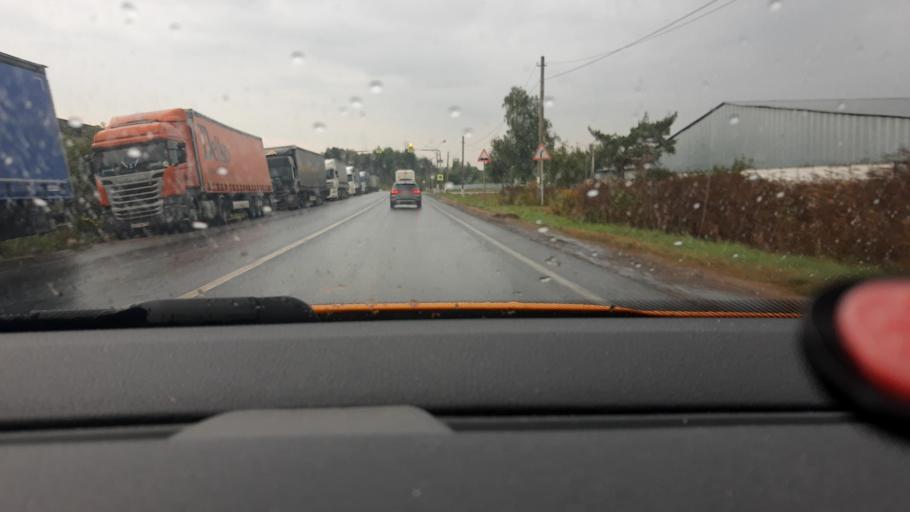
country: RU
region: Moskovskaya
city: Obukhovo
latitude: 55.8205
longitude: 38.2609
